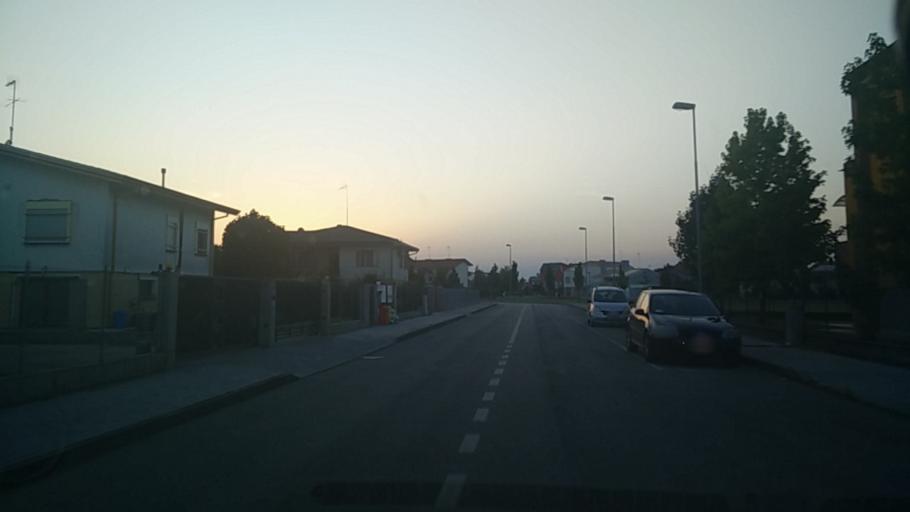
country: IT
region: Veneto
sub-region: Provincia di Venezia
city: San Dona di Piave
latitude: 45.6435
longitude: 12.5641
